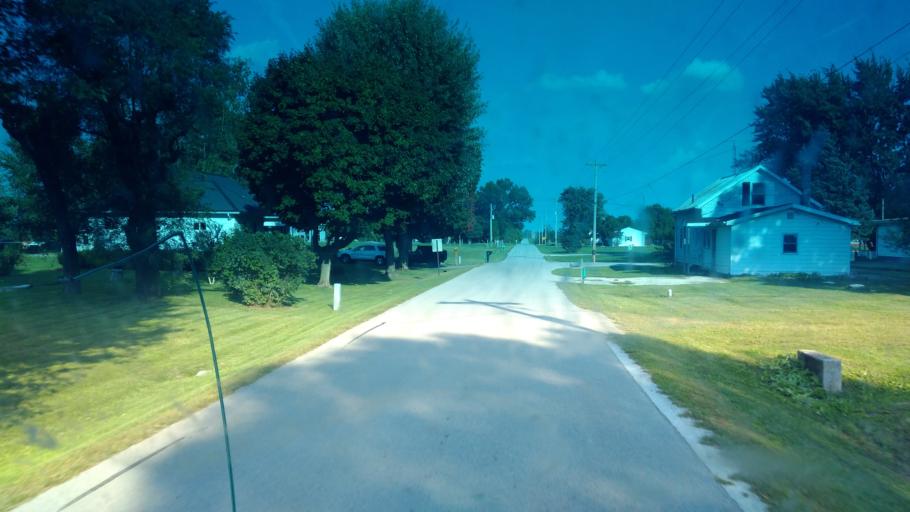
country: US
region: Ohio
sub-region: Wyandot County
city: Carey
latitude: 40.9200
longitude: -83.3441
